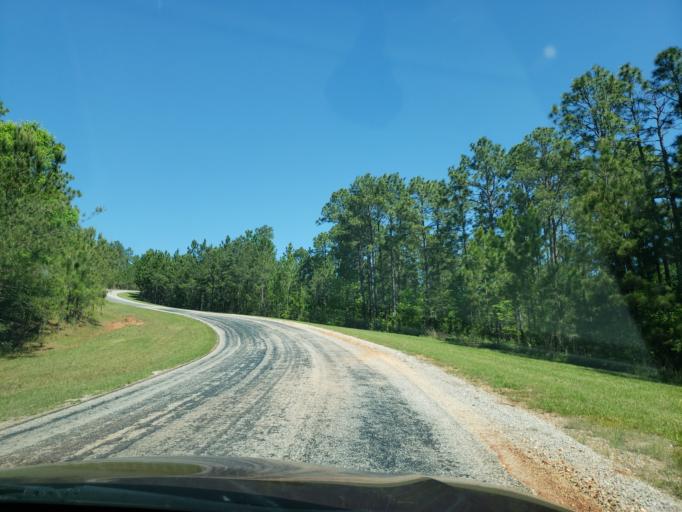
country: US
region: Alabama
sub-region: Elmore County
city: Eclectic
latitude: 32.6821
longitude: -85.9013
